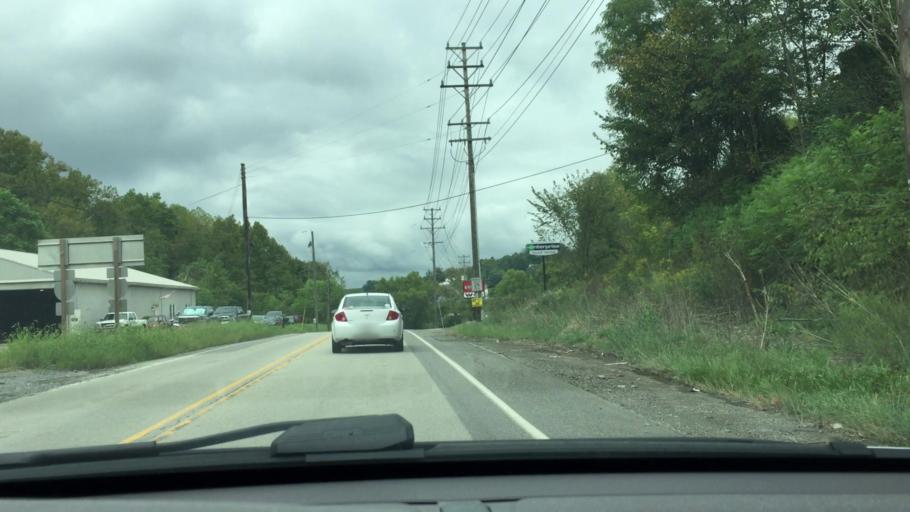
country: US
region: Pennsylvania
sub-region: Washington County
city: Houston
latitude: 40.2465
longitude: -80.2036
